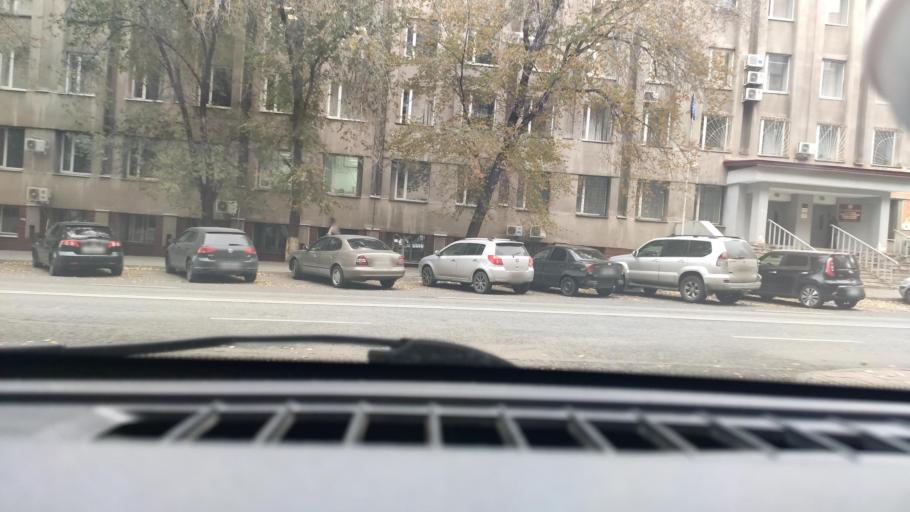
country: RU
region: Samara
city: Samara
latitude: 53.2090
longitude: 50.1262
